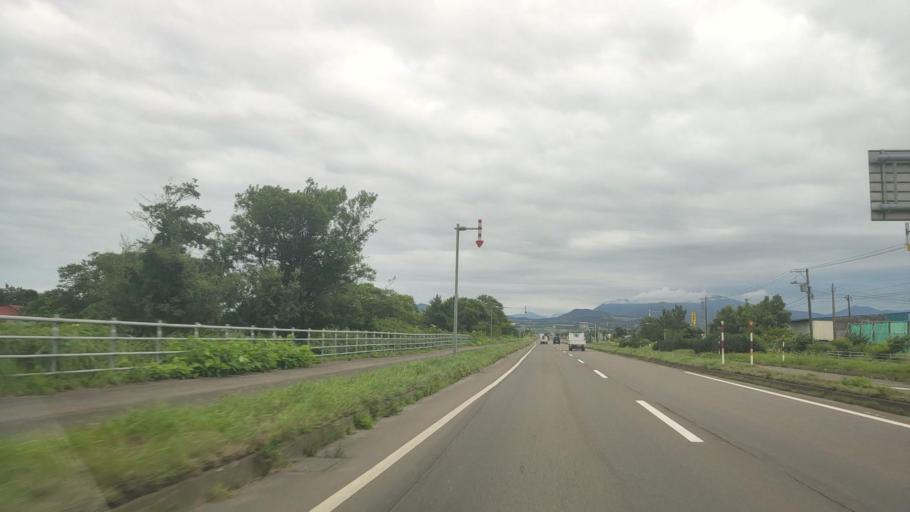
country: JP
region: Hokkaido
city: Nanae
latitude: 42.2778
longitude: 140.2721
